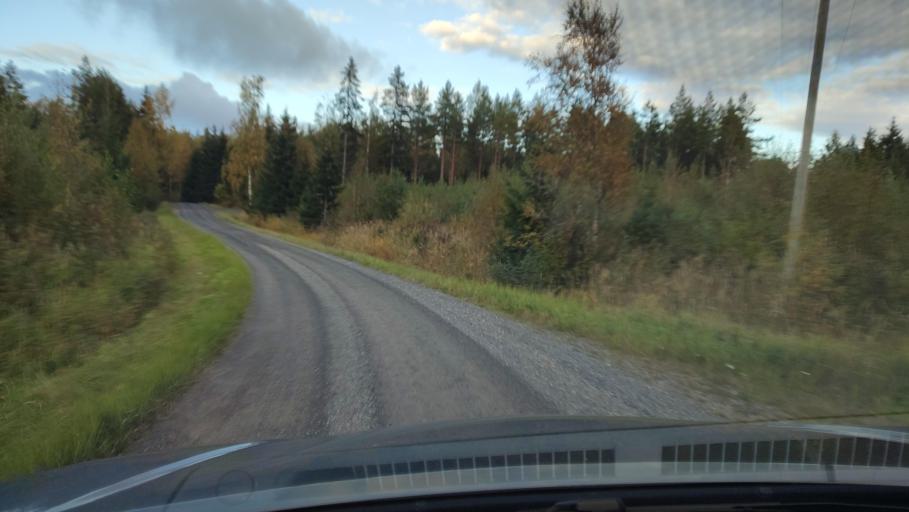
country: FI
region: Ostrobothnia
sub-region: Sydosterbotten
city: Kristinestad
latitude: 62.2313
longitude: 21.4309
